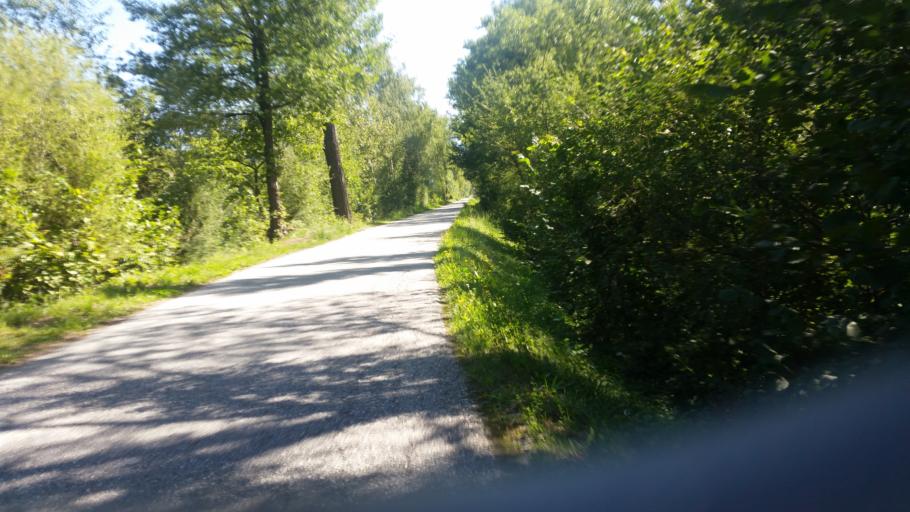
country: CH
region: Valais
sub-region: Sierre District
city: Chermignon-d'en Haut
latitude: 46.2717
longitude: 7.4857
